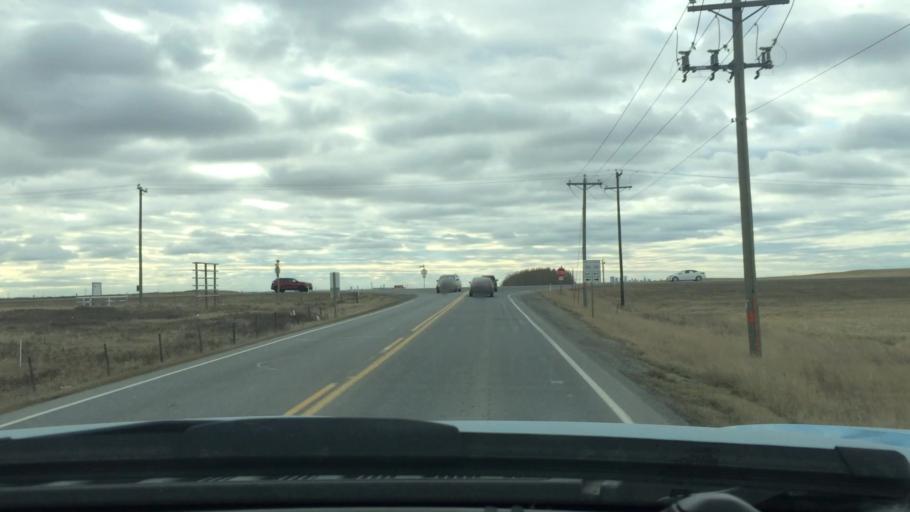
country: CA
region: Alberta
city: Airdrie
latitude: 51.2134
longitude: -114.0250
